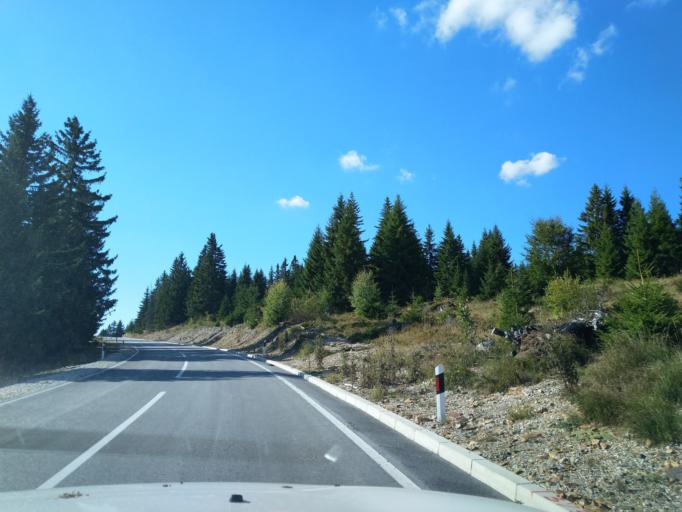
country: RS
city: Sokolovica
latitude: 43.3105
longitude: 20.2981
